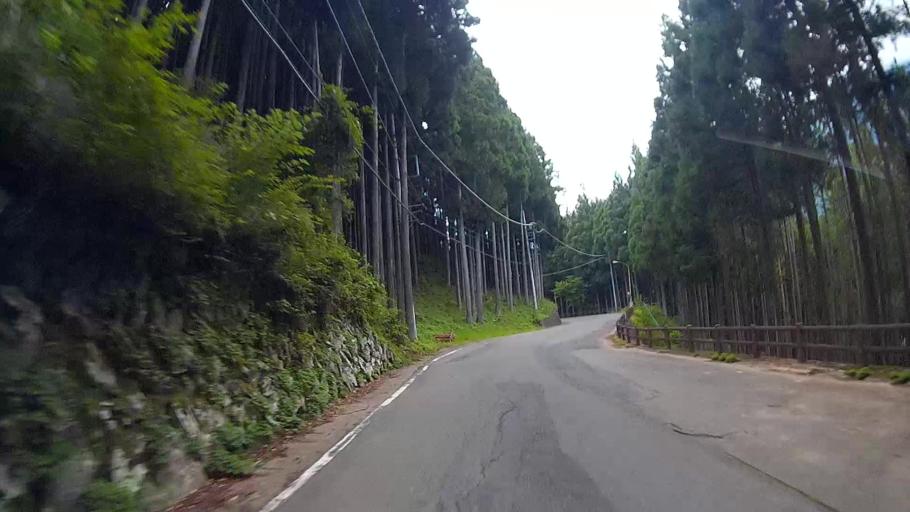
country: JP
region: Saitama
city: Chichibu
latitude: 35.9422
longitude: 138.8731
